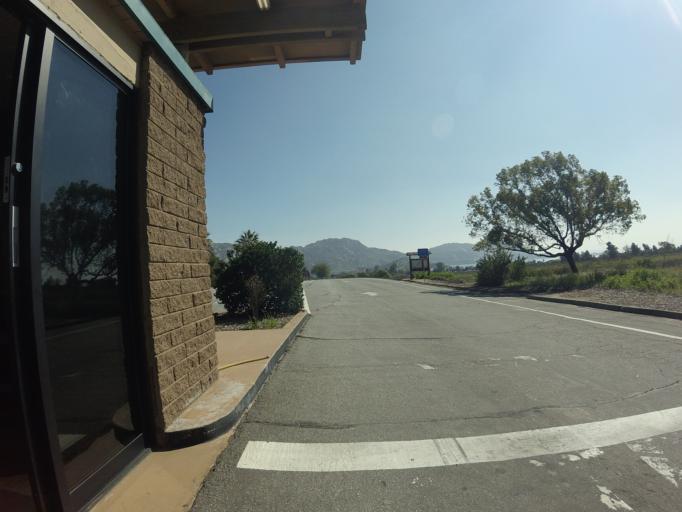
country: US
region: California
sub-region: Riverside County
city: Lakeview
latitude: 33.8811
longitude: -117.1725
